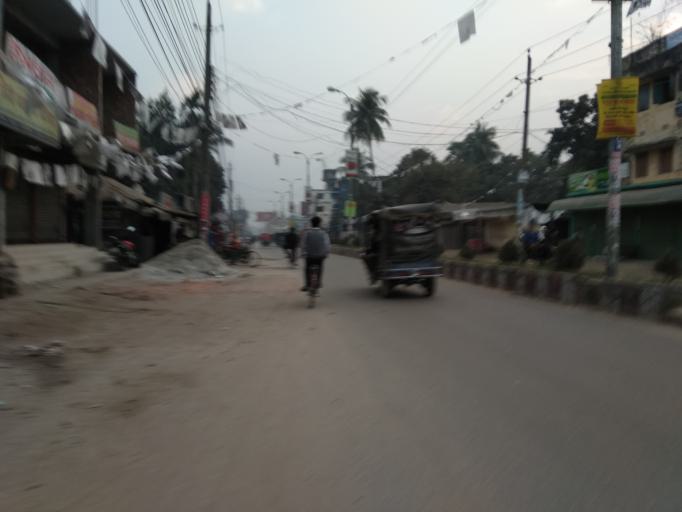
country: BD
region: Rangpur Division
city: Rangpur
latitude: 25.7365
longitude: 89.2548
